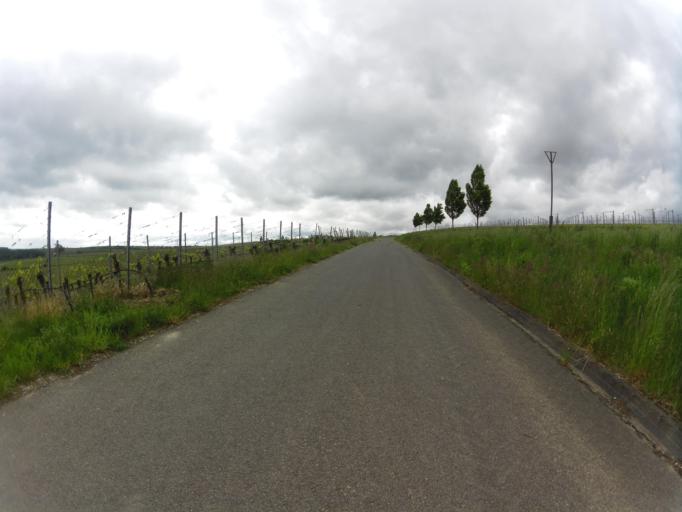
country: DE
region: Bavaria
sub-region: Regierungsbezirk Unterfranken
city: Sommerach
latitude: 49.8386
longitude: 10.2080
